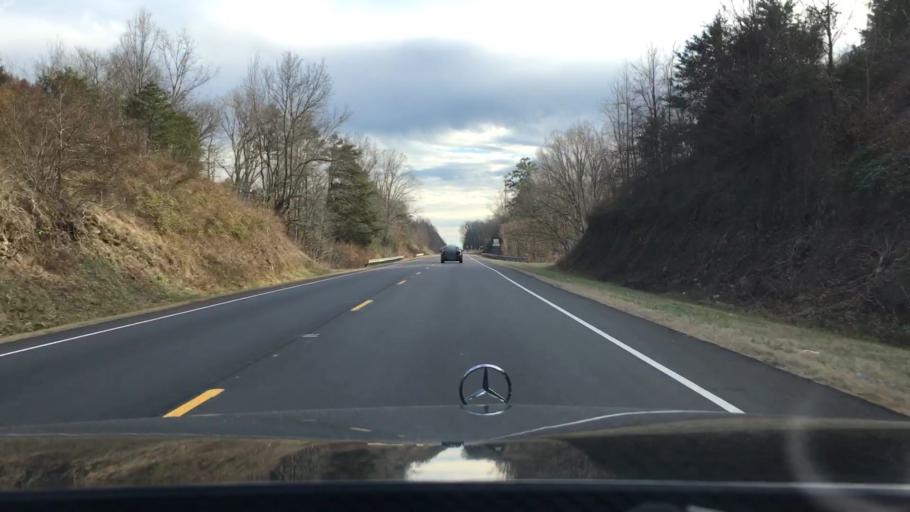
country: US
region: Virginia
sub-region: City of Danville
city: Danville
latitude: 36.4964
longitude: -79.3859
